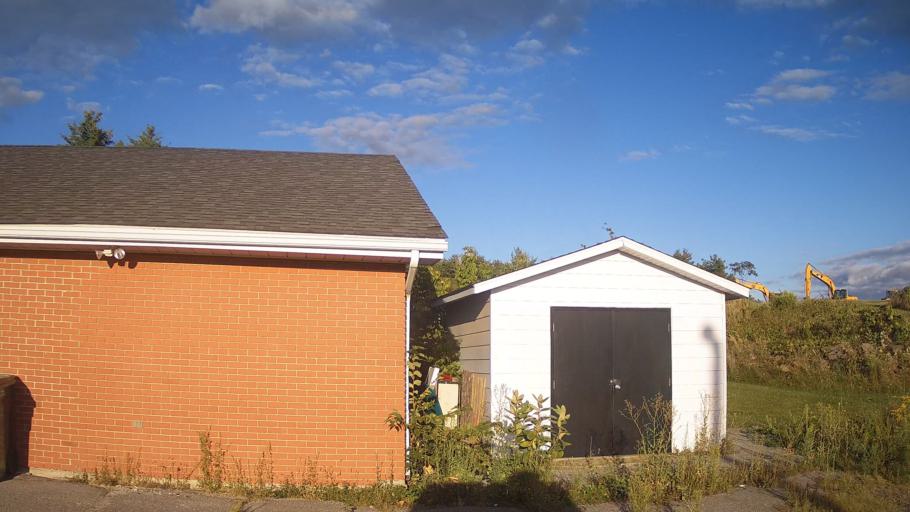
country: CA
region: Ontario
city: Gananoque
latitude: 44.3478
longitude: -76.1709
